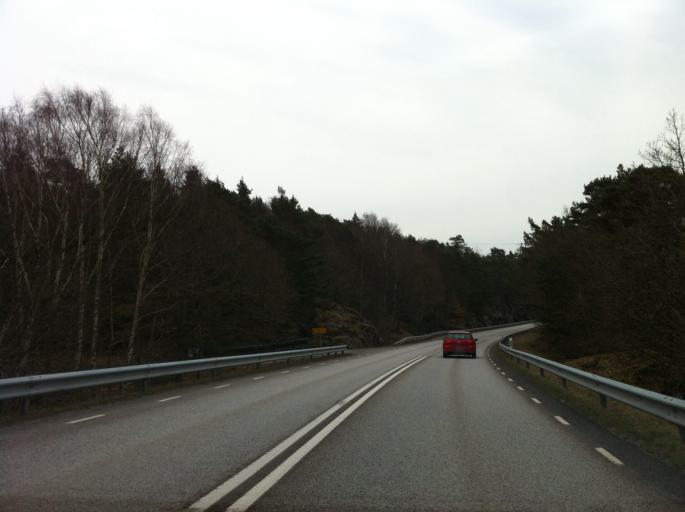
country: SE
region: Vaestra Goetaland
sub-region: Orust
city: Henan
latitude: 58.2779
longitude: 11.6938
